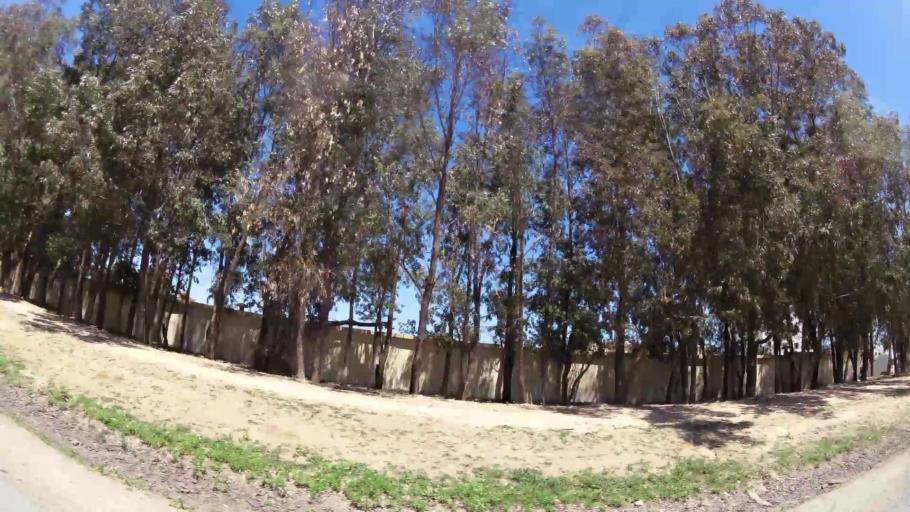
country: MA
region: Meknes-Tafilalet
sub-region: Meknes
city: Meknes
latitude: 33.8482
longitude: -5.5545
